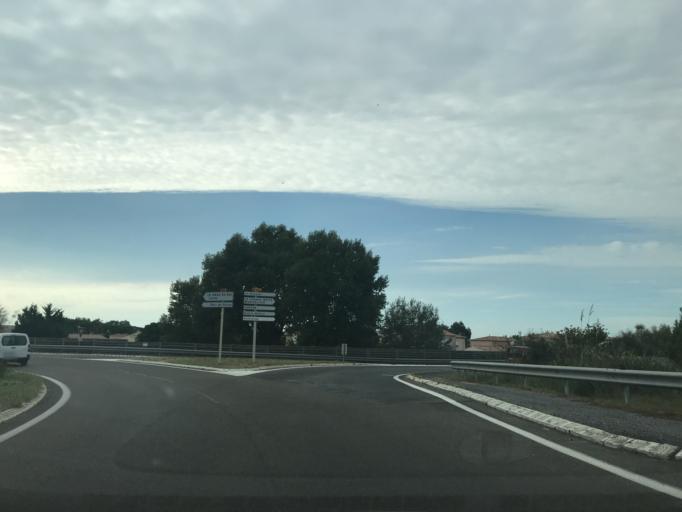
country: FR
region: Languedoc-Roussillon
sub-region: Departement du Gard
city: Le Grau-du-Roi
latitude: 43.5492
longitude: 4.1342
